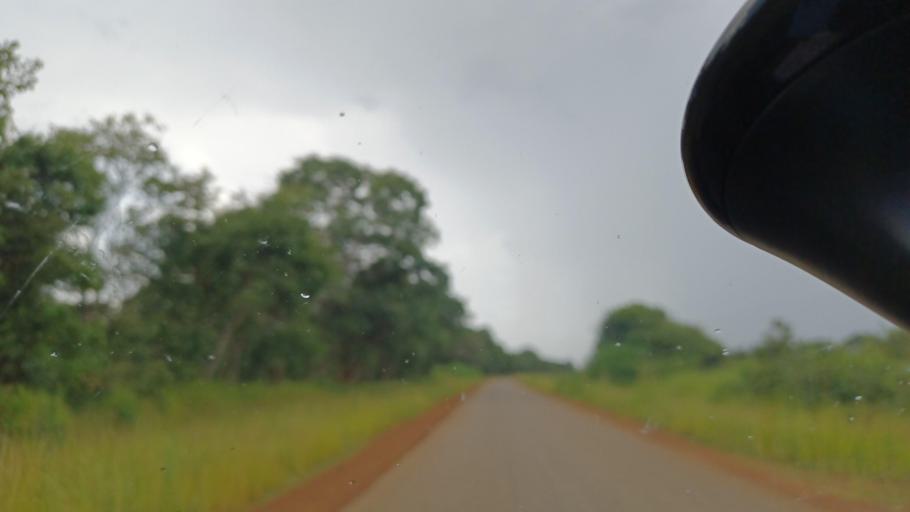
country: ZM
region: North-Western
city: Kasempa
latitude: -13.0448
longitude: 25.9919
